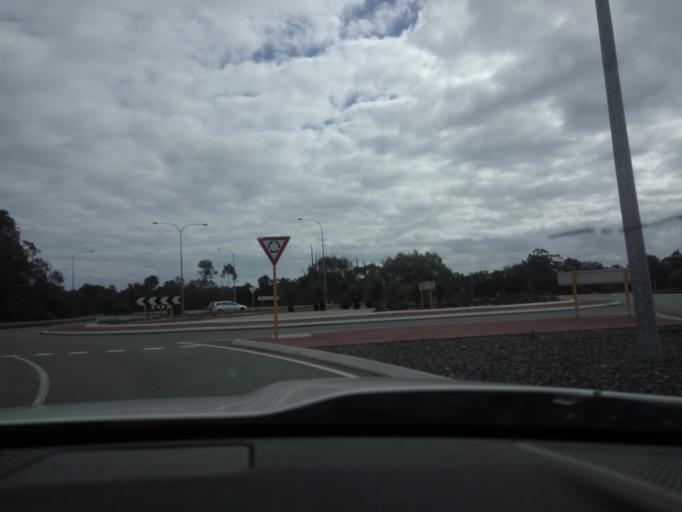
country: AU
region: Western Australia
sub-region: City of Cockburn
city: Bibra Lake
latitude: -32.1026
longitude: 115.8243
